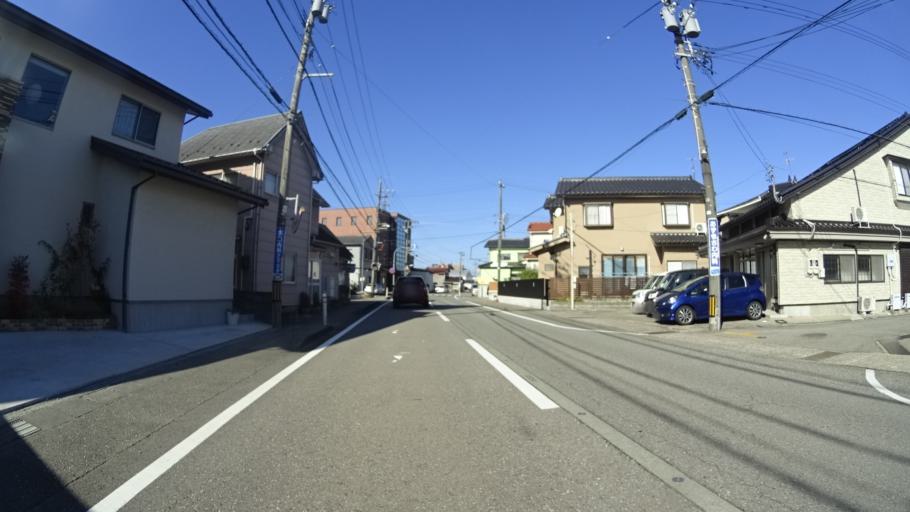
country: JP
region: Ishikawa
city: Kanazawa-shi
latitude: 36.6010
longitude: 136.6078
